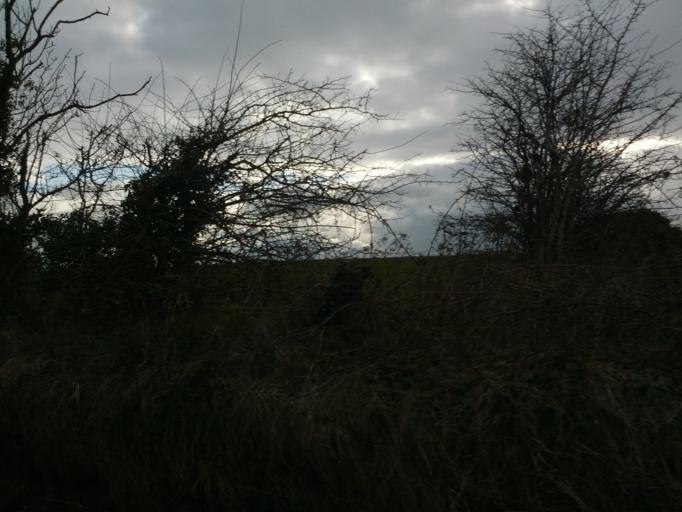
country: IE
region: Connaught
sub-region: County Galway
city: Athenry
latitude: 53.4053
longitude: -8.6341
